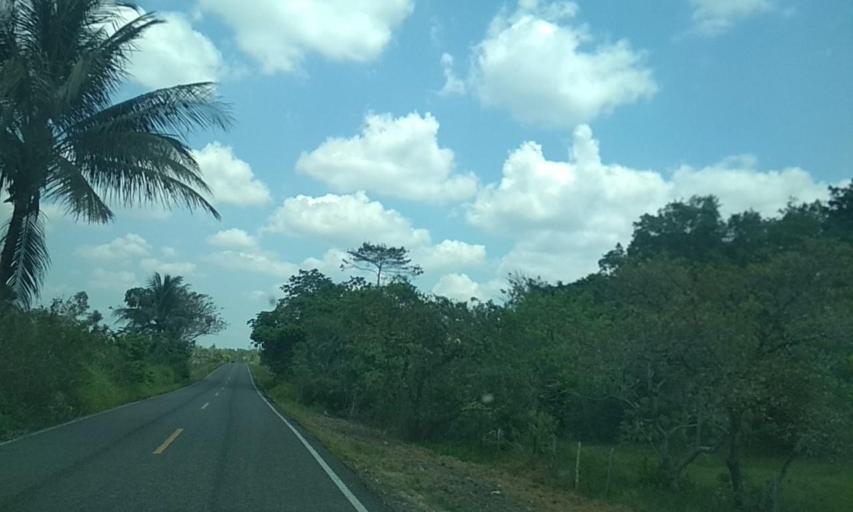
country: MX
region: Tabasco
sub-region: Huimanguillo
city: Huapacal 1ra. Seccion
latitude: 17.7532
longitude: -93.7374
